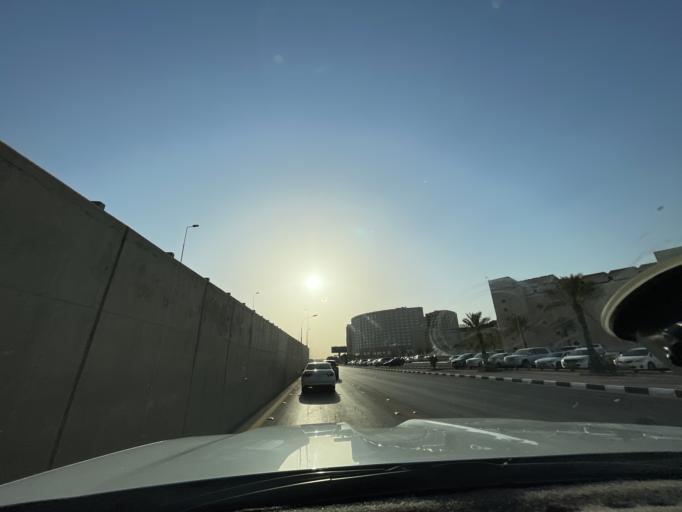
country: SA
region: Eastern Province
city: Khobar
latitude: 26.2889
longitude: 50.1815
